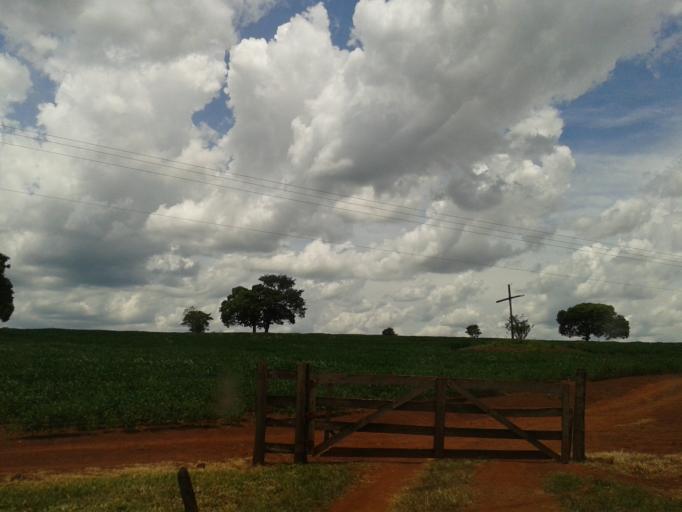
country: BR
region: Minas Gerais
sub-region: Centralina
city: Centralina
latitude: -18.7046
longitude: -49.2199
